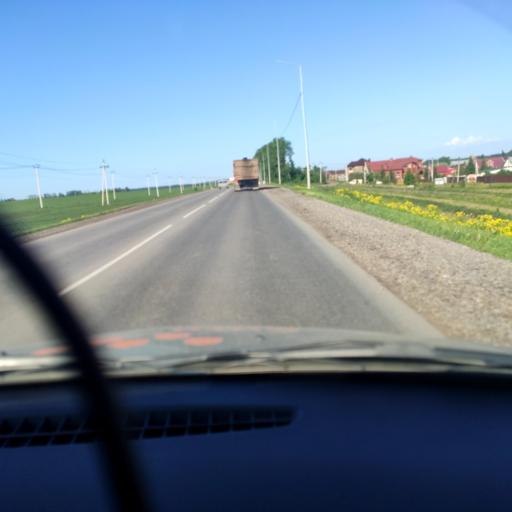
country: RU
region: Bashkortostan
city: Avdon
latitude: 54.6077
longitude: 55.8607
